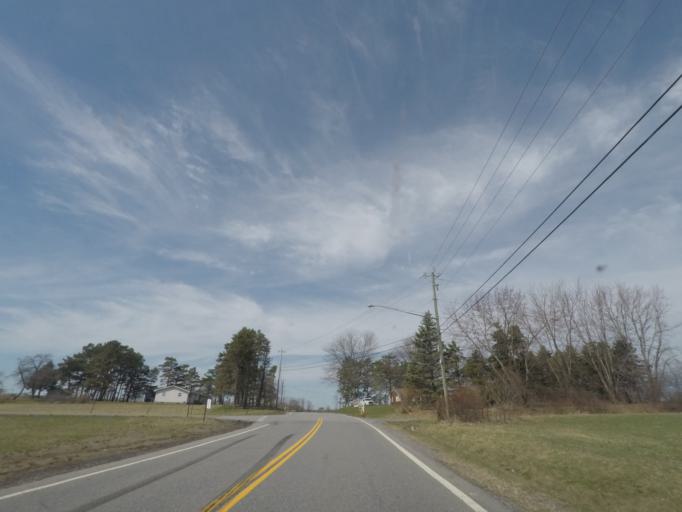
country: US
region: New York
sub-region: Saratoga County
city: Mechanicville
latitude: 42.9049
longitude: -73.7254
